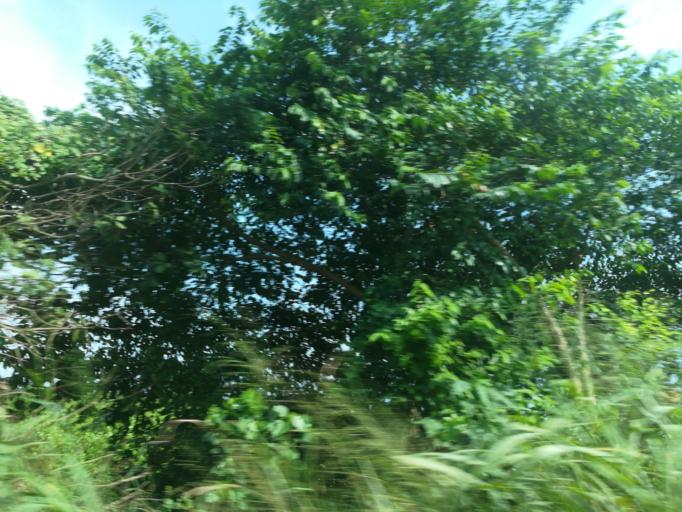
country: NG
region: Lagos
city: Ikorodu
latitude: 6.6127
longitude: 3.6425
